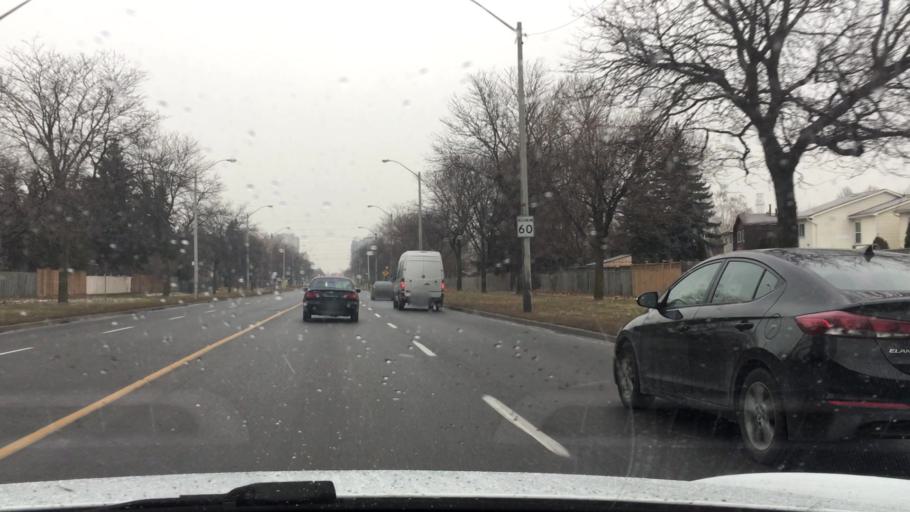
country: CA
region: Ontario
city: Scarborough
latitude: 43.8128
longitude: -79.2696
